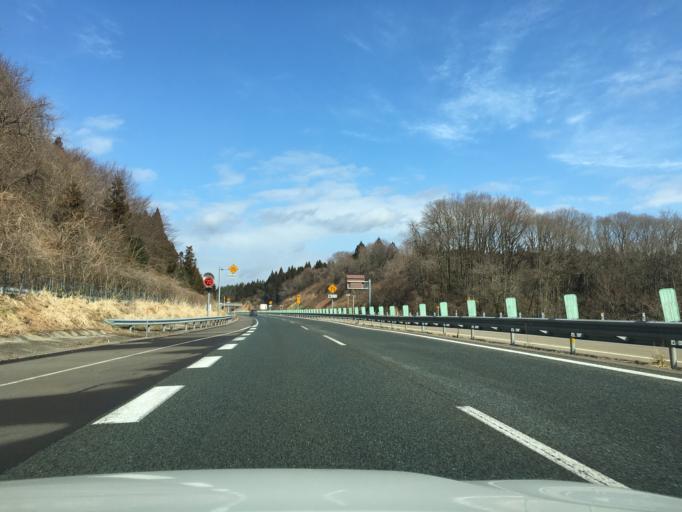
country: JP
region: Akita
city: Akita
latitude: 39.7251
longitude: 140.1809
